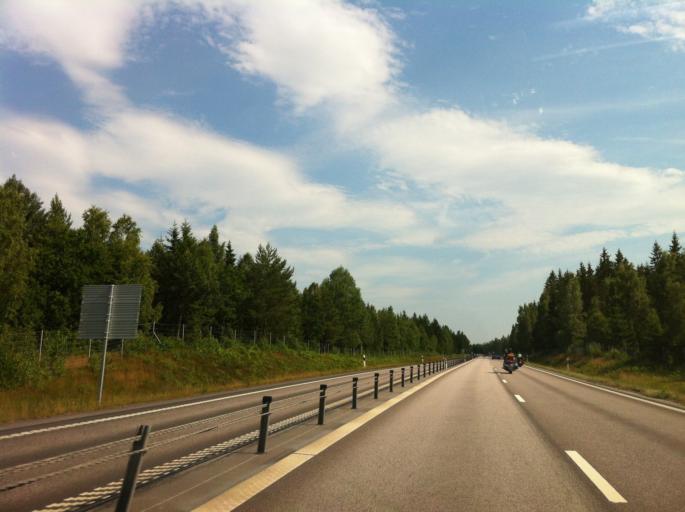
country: SE
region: Kalmar
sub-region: Kalmar Kommun
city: Trekanten
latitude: 56.7078
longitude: 16.0839
